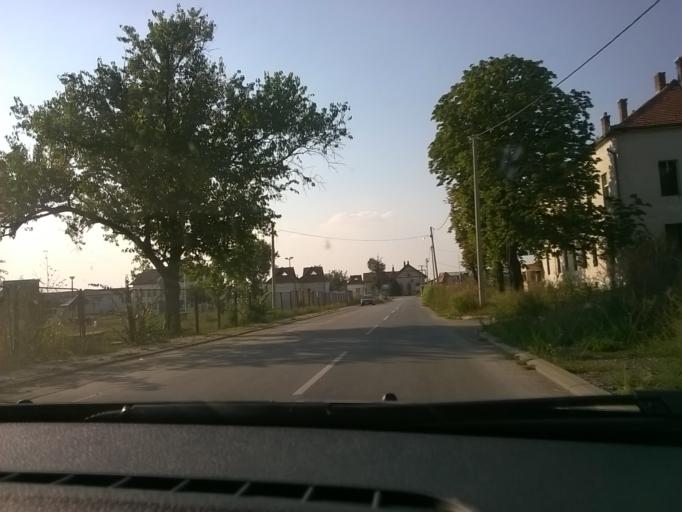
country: RS
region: Autonomna Pokrajina Vojvodina
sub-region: Juznobanatski Okrug
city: Vrsac
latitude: 45.1300
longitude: 21.2846
